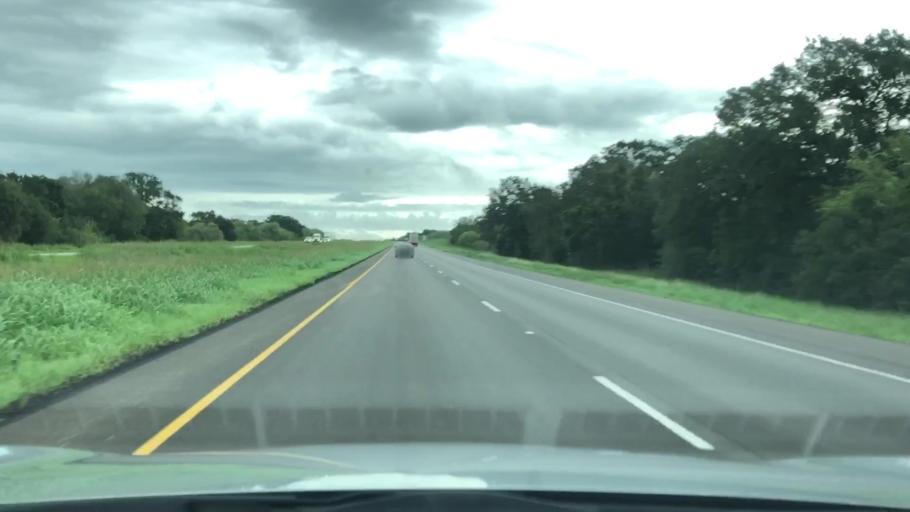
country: US
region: Texas
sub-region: Gonzales County
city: Gonzales
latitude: 29.6496
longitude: -97.4957
